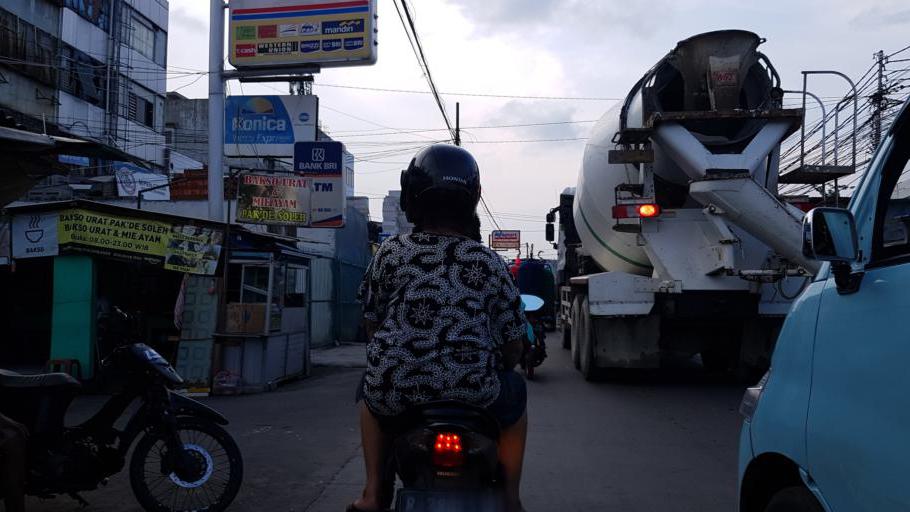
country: ID
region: West Java
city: Ciputat
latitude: -6.1344
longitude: 106.7507
